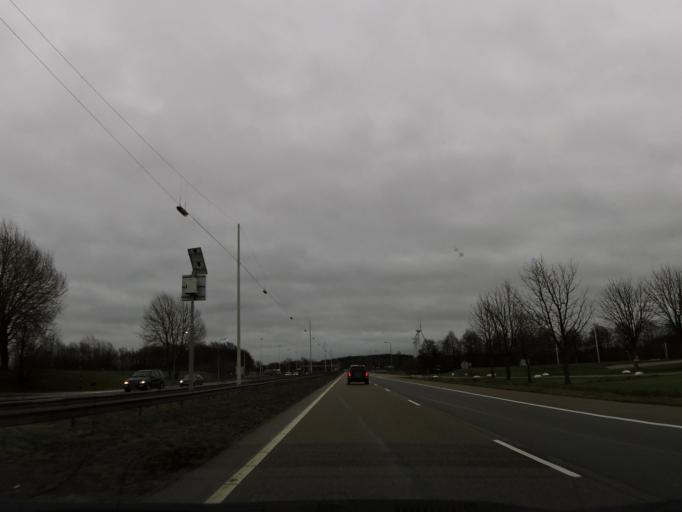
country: NL
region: Limburg
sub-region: Gemeente Simpelveld
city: Simpelveld
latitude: 50.8230
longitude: 6.0202
